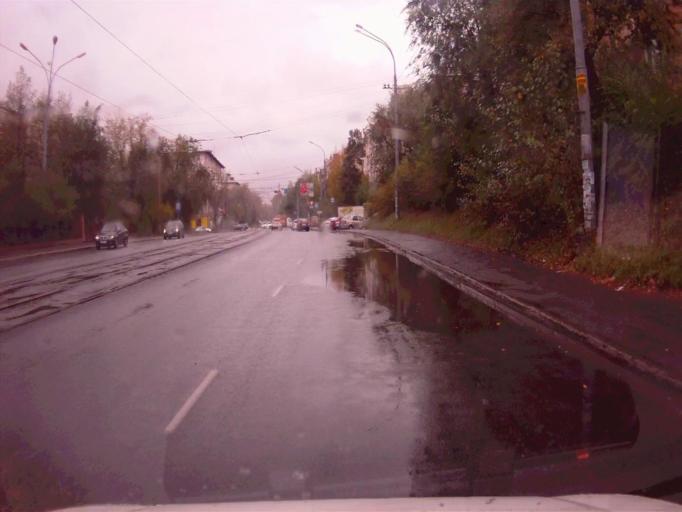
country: RU
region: Chelyabinsk
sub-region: Gorod Chelyabinsk
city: Chelyabinsk
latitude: 55.1842
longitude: 61.4144
